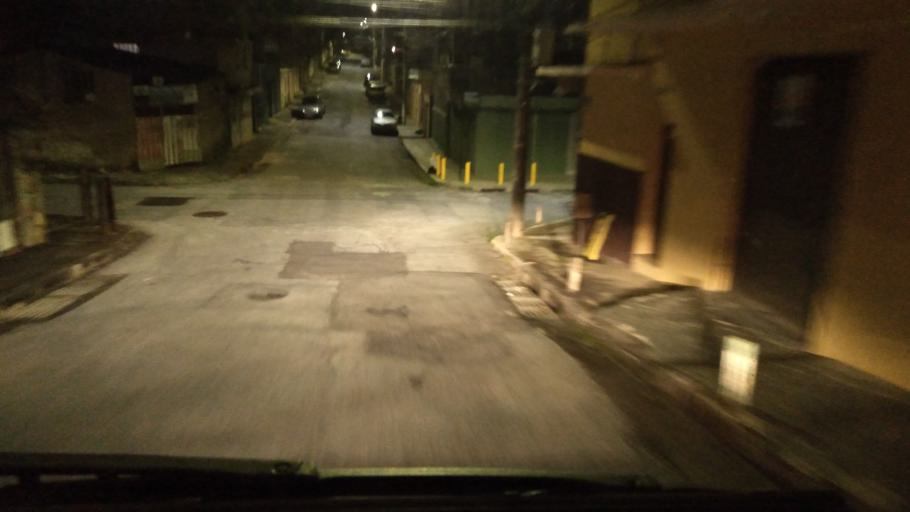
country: BR
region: Minas Gerais
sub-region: Belo Horizonte
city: Belo Horizonte
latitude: -19.8980
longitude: -43.9716
